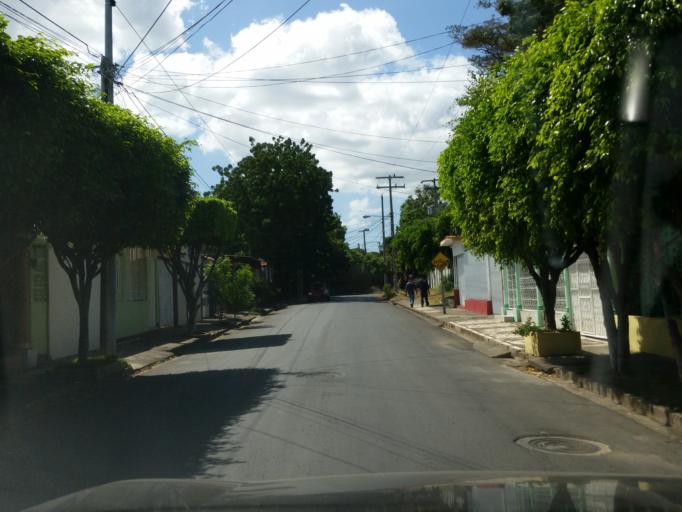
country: NI
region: Managua
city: Managua
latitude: 12.1203
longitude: -86.2313
